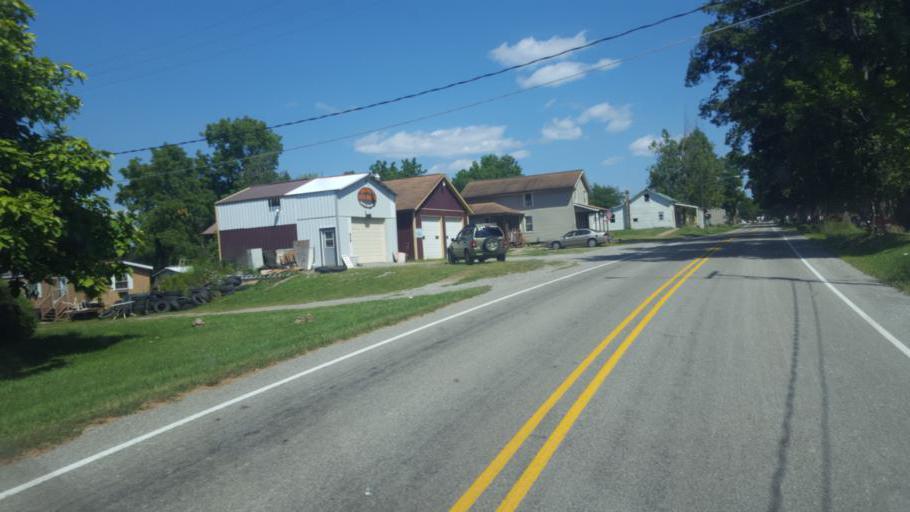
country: US
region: Pennsylvania
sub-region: Clarion County
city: Knox
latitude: 41.1260
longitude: -79.5615
